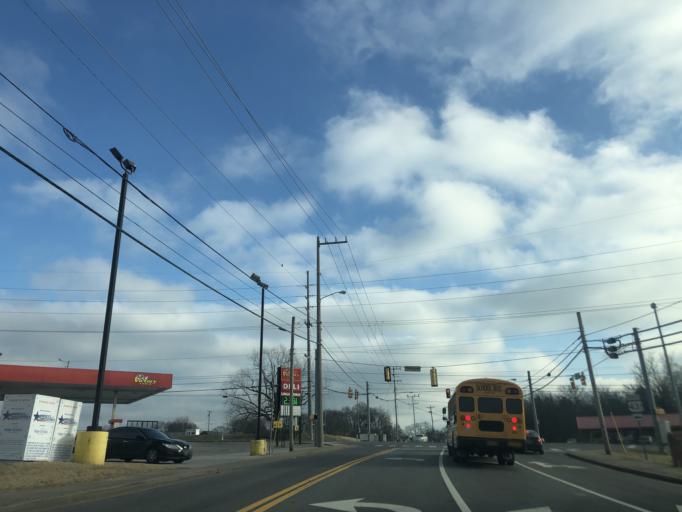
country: US
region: Tennessee
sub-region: Davidson County
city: Nashville
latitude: 36.2076
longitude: -86.7921
